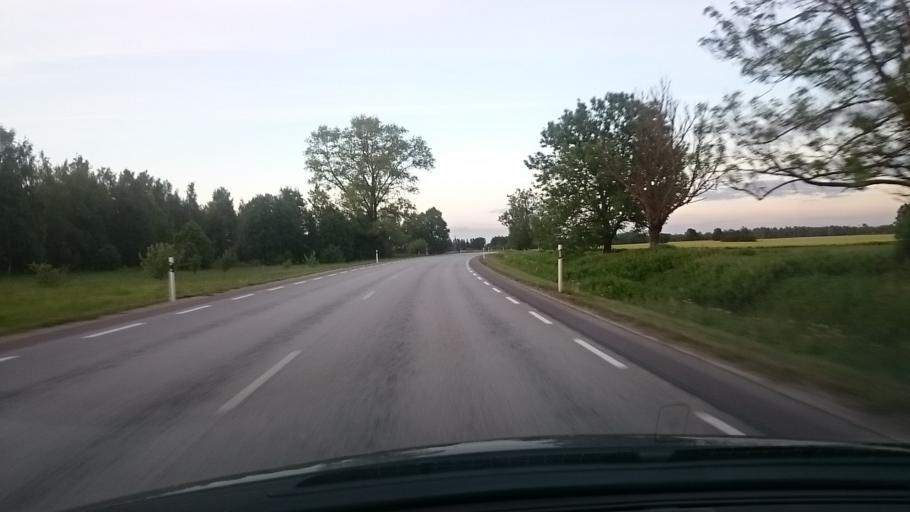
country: EE
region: Viljandimaa
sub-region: Vohma linn
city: Vohma
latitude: 58.6523
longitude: 25.5910
